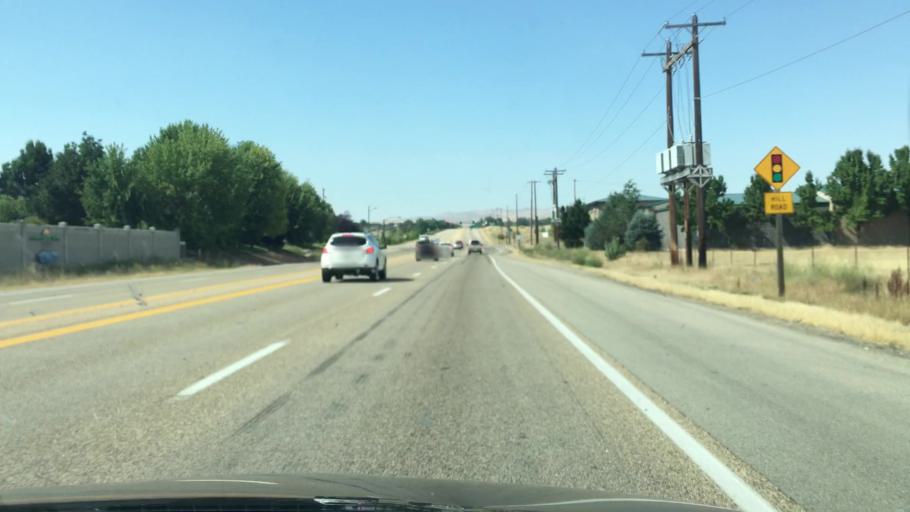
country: US
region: Idaho
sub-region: Ada County
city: Eagle
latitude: 43.6914
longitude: -116.3192
